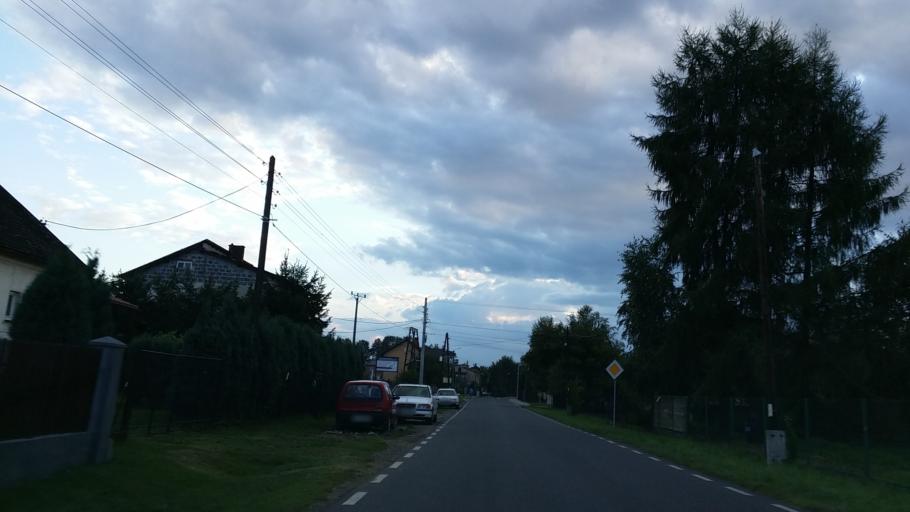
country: PL
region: Lesser Poland Voivodeship
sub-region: Powiat oswiecimski
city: Nowa Wies
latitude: 49.9084
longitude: 19.2266
